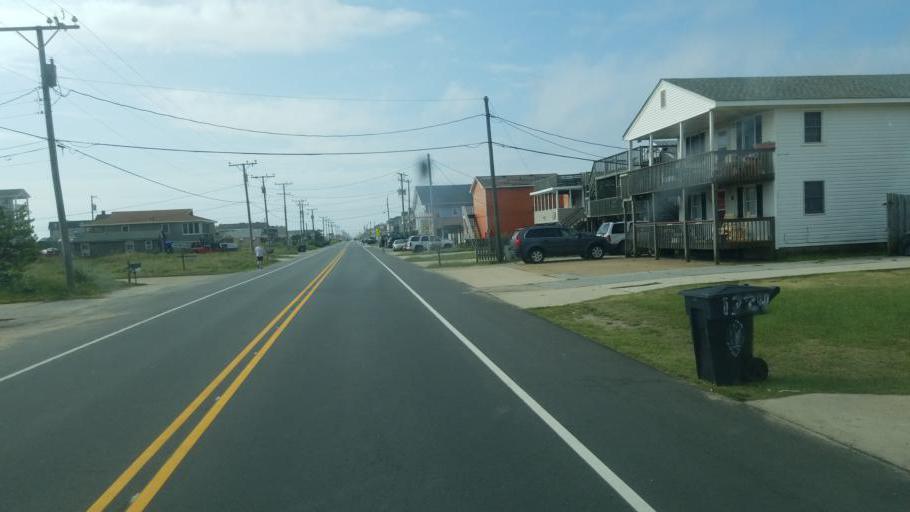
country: US
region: North Carolina
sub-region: Dare County
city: Kill Devil Hills
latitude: 36.0042
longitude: -75.6515
